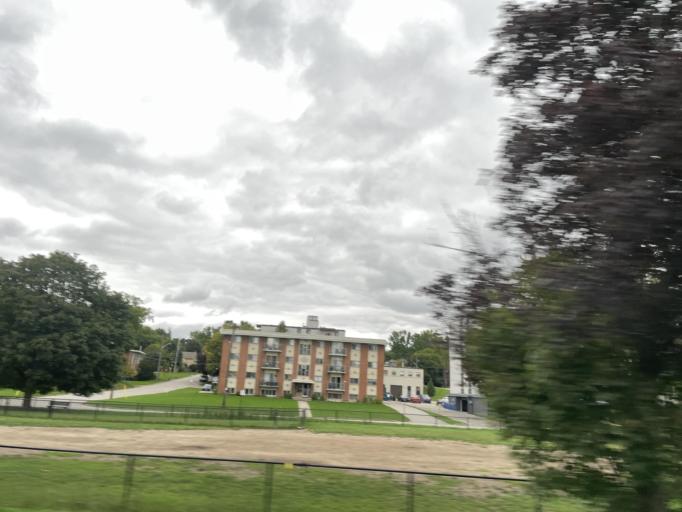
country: CA
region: Ontario
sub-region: Wellington County
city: Guelph
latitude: 43.5330
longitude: -80.2559
